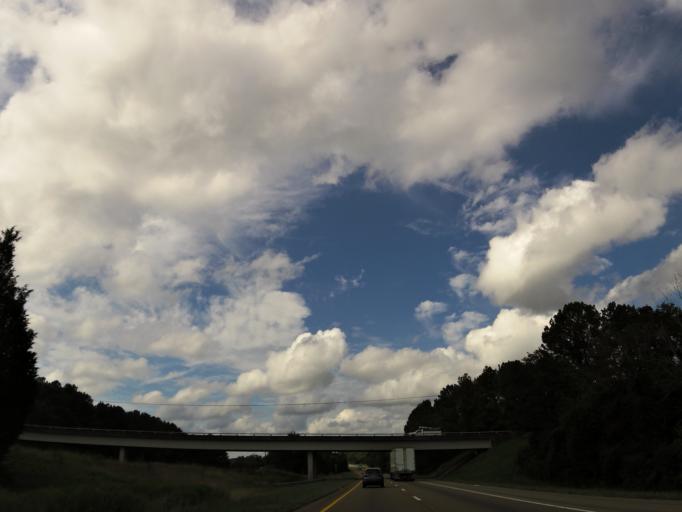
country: US
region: Tennessee
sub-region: Loudon County
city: Loudon
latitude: 35.7842
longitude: -84.3433
